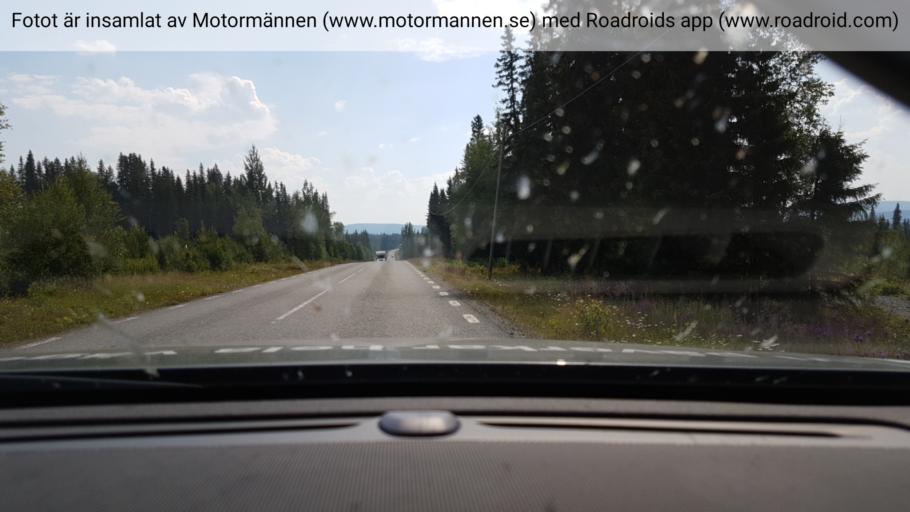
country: SE
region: Vaesterbotten
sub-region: Vilhelmina Kommun
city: Sjoberg
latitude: 65.4593
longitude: 16.0867
